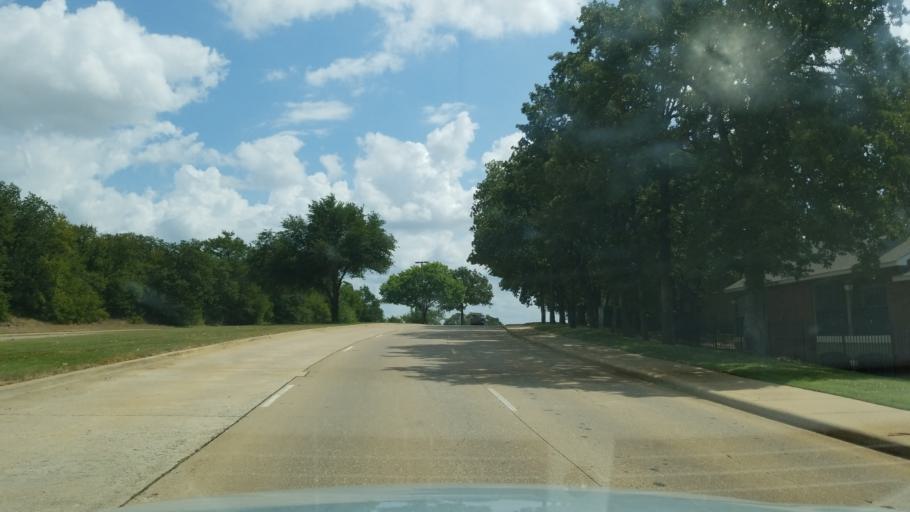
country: US
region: Texas
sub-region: Tarrant County
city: Euless
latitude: 32.8696
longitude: -97.0721
